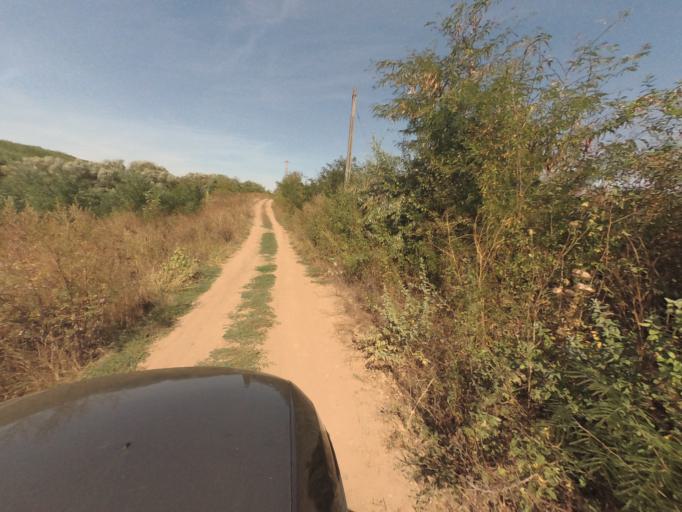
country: RO
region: Vaslui
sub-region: Comuna Costesti
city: Costesti
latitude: 46.5168
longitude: 27.7423
